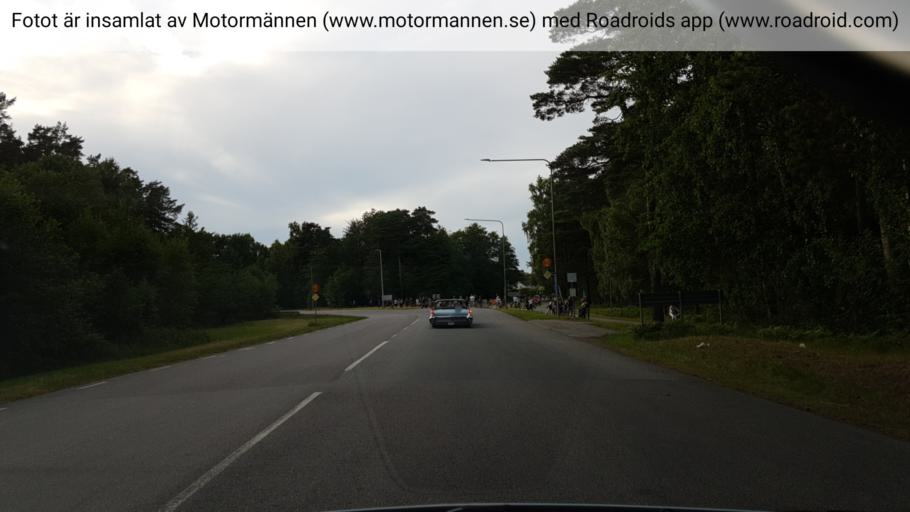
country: SE
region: Vaestra Goetaland
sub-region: Lidkopings Kommun
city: Lidkoping
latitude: 58.5170
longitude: 13.1310
